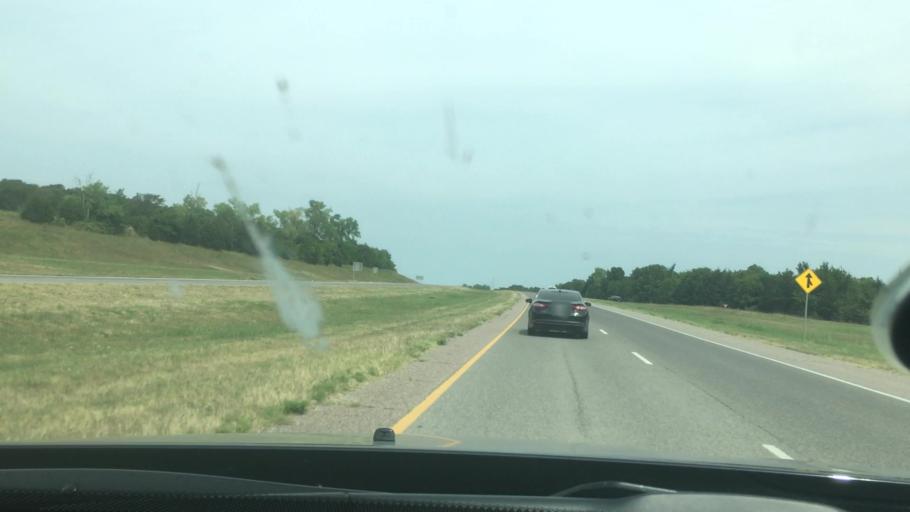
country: US
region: Oklahoma
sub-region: Pontotoc County
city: Ada
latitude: 34.7386
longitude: -96.6449
